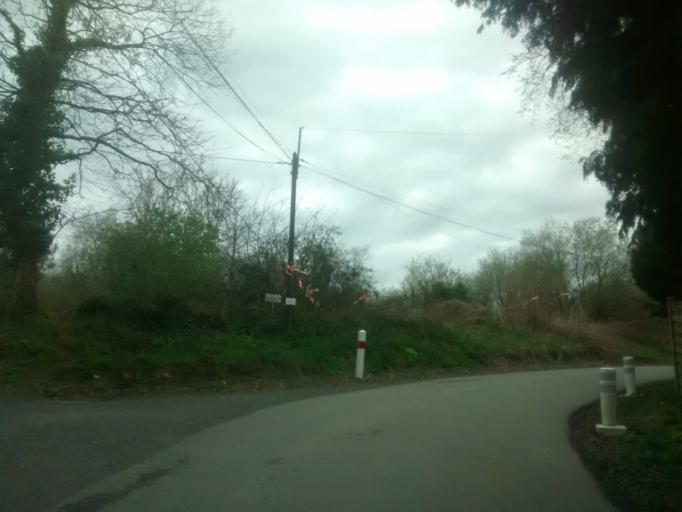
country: FR
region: Brittany
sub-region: Departement d'Ille-et-Vilaine
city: Erce-pres-Liffre
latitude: 48.2393
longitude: -1.5175
